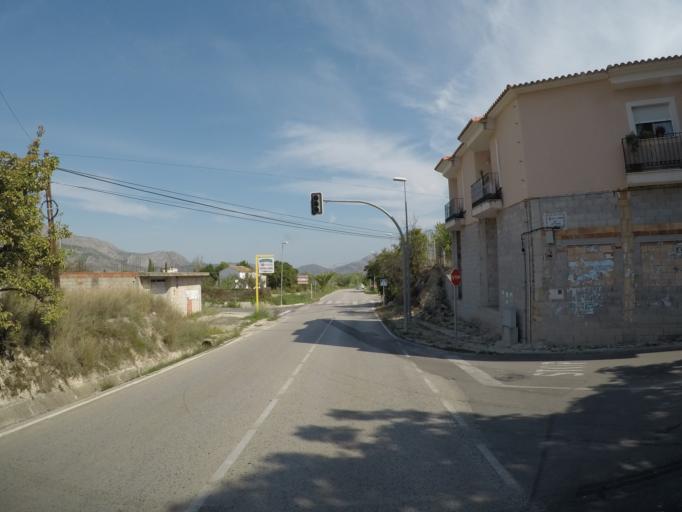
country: ES
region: Valencia
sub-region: Provincia de Alicante
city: Orba
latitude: 38.7800
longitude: -0.0659
